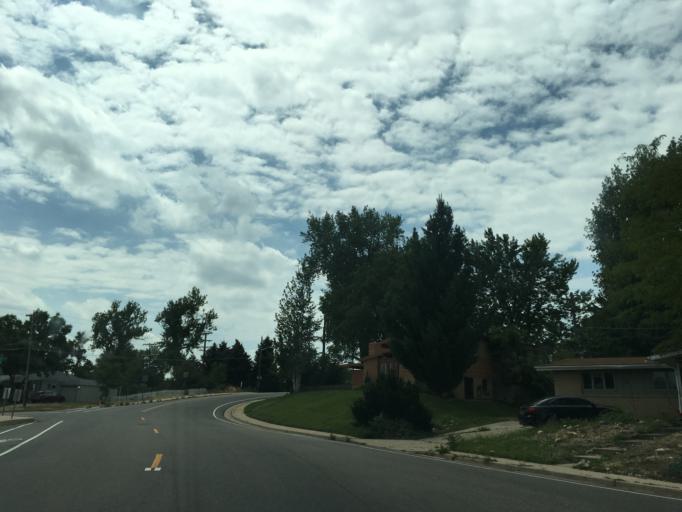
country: US
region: Colorado
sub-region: Arapahoe County
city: Sheridan
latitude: 39.6661
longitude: -105.0350
